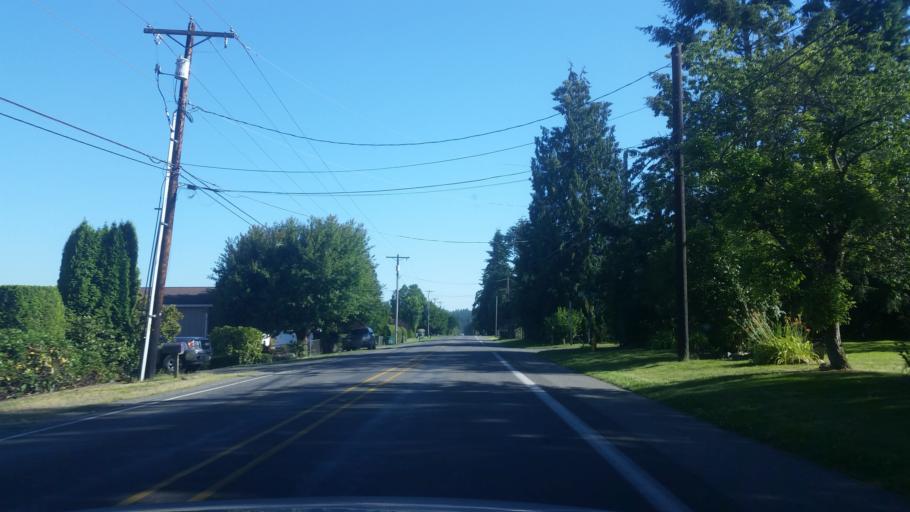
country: US
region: Washington
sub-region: Snohomish County
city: Cathcart
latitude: 47.8595
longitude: -122.0991
